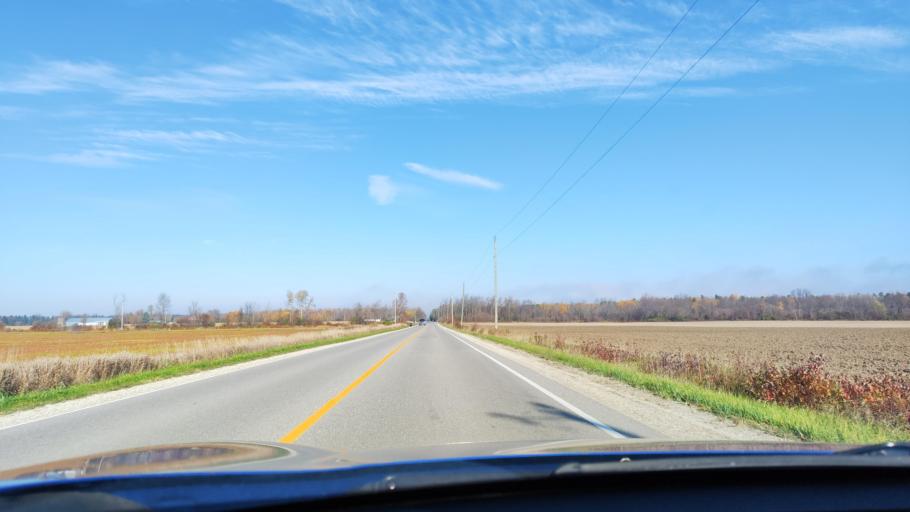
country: CA
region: Ontario
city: Wasaga Beach
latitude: 44.3981
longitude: -80.0574
